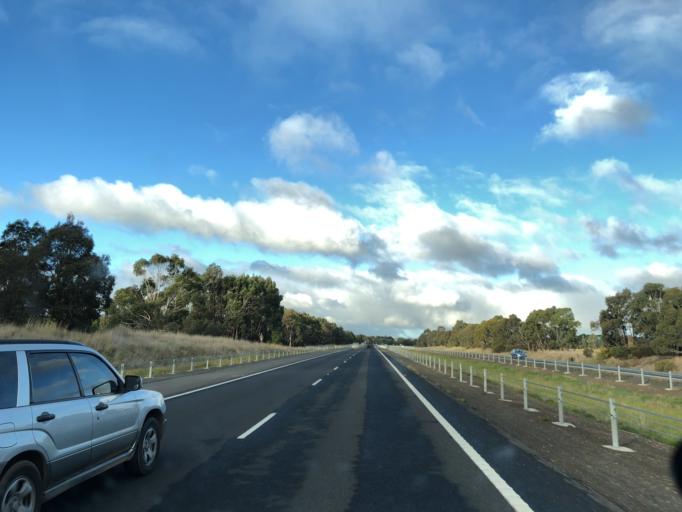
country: AU
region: Victoria
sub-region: Mount Alexander
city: Castlemaine
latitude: -37.2254
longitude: 144.4300
